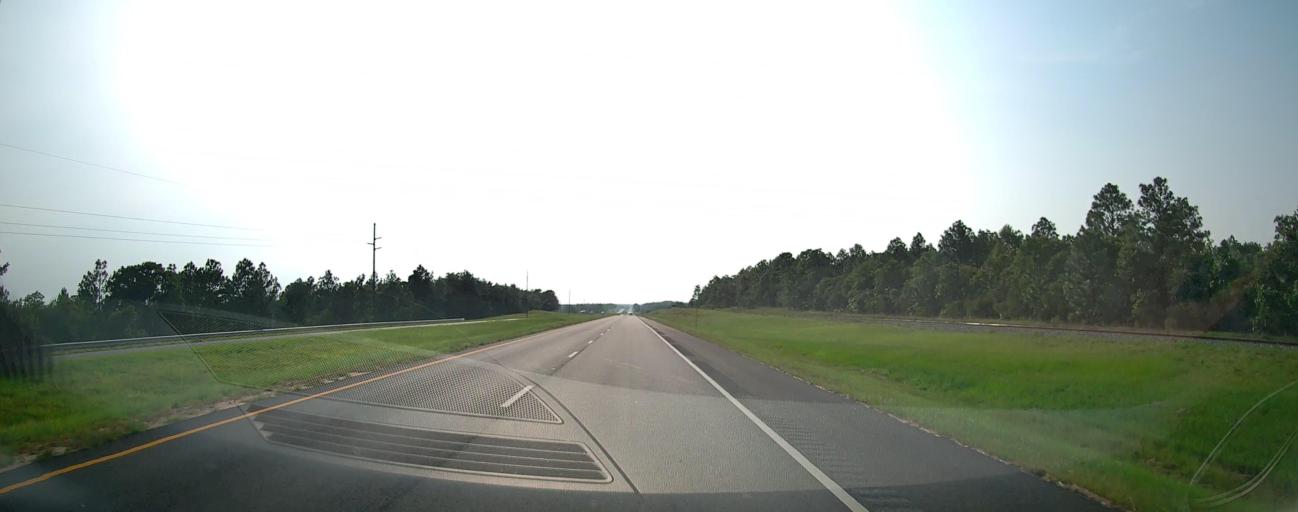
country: US
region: Georgia
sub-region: Taylor County
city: Butler
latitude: 32.5811
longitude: -84.3244
